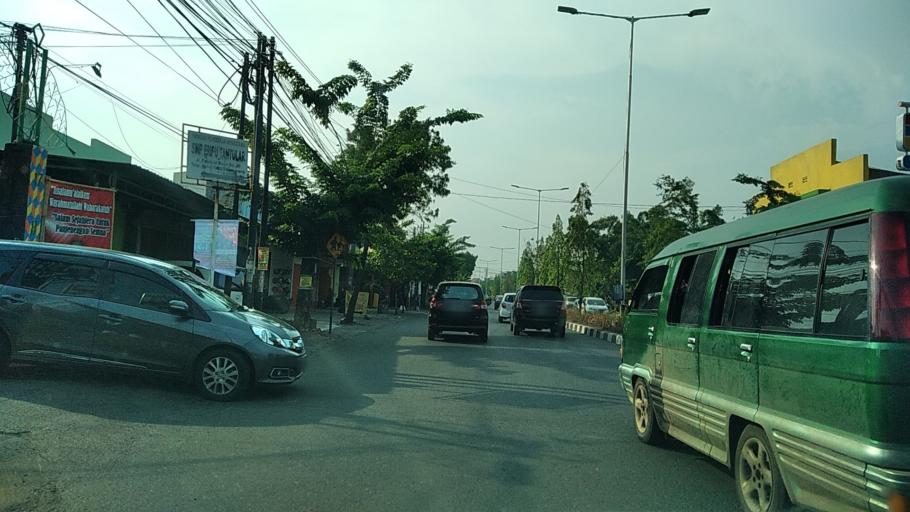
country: ID
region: Central Java
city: Semarang
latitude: -7.0040
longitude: 110.4690
